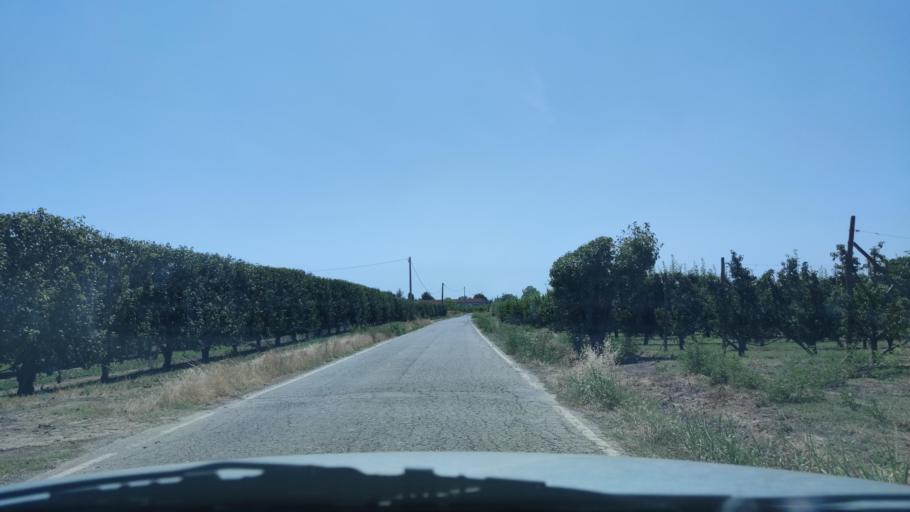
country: ES
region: Catalonia
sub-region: Provincia de Lleida
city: Torrefarrera
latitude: 41.6558
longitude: 0.5935
